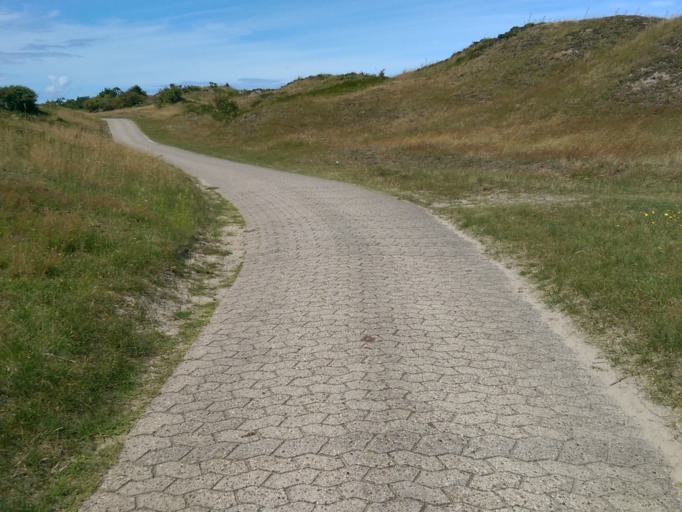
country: DE
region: Lower Saxony
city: Spiekeroog
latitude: 53.7718
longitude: 7.7231
